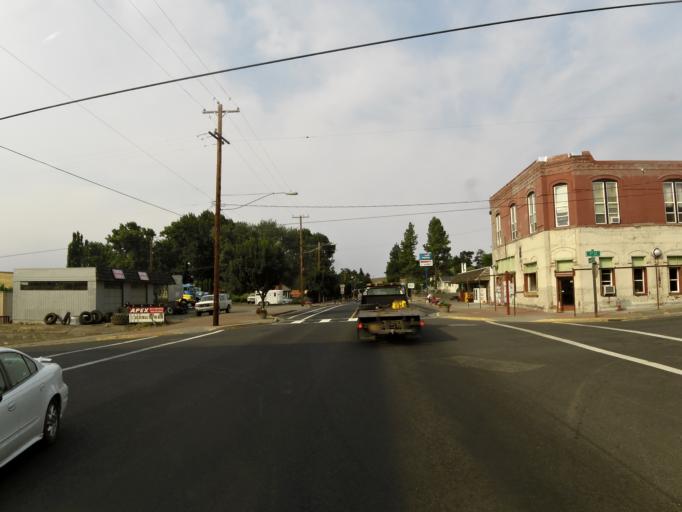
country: US
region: Oregon
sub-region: Sherman County
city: Moro
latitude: 45.4842
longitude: -120.7303
